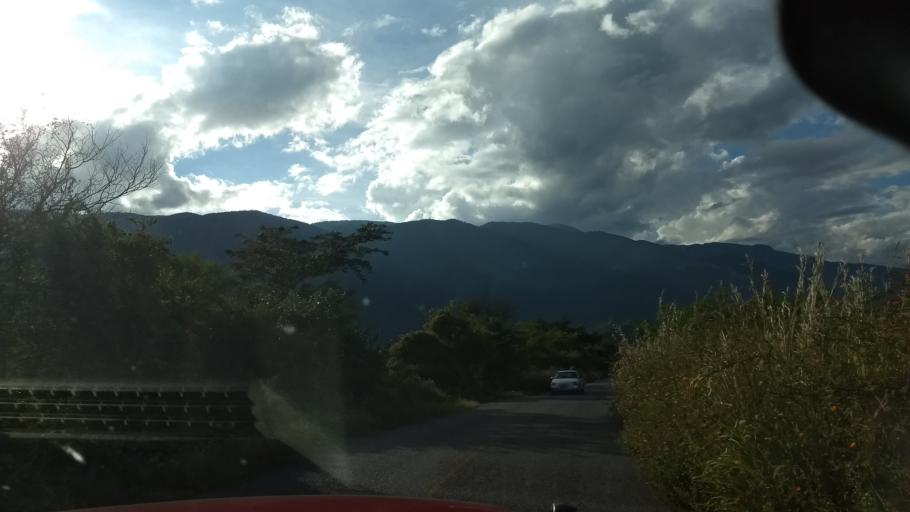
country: MX
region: Colima
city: Suchitlan
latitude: 19.4486
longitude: -103.8155
